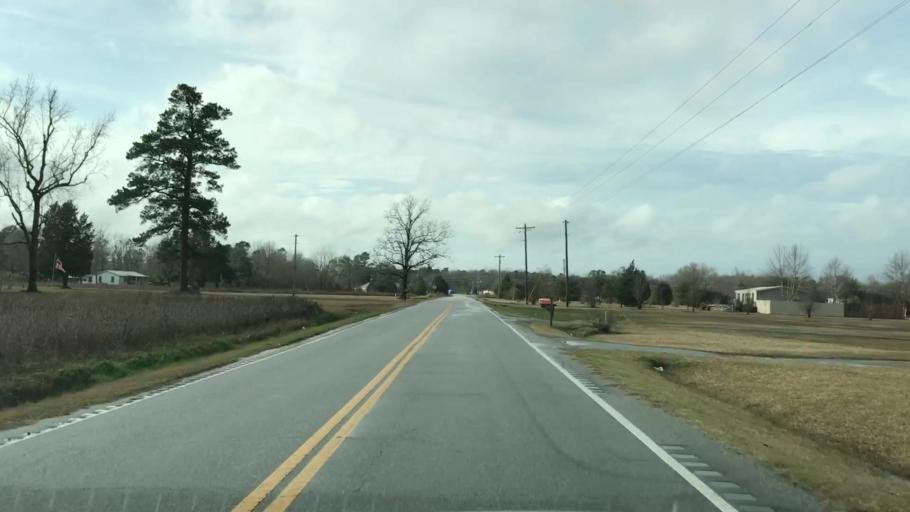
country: US
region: South Carolina
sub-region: Williamsburg County
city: Andrews
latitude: 33.5019
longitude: -79.5191
